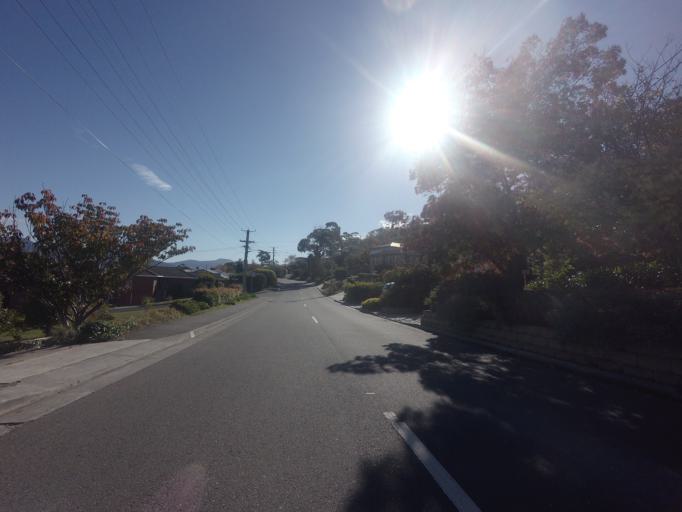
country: AU
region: Tasmania
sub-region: Clarence
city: Lindisfarne
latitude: -42.8468
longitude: 147.3426
